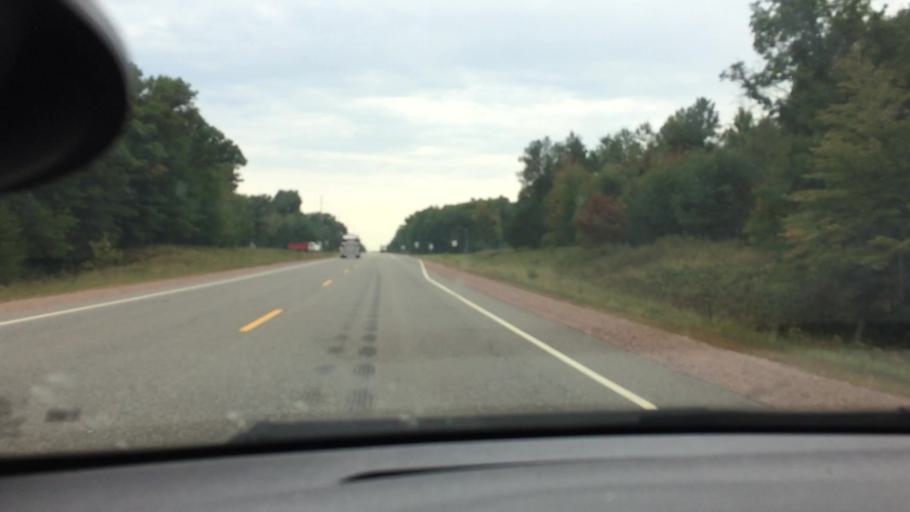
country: US
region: Wisconsin
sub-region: Clark County
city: Neillsville
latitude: 44.5714
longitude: -90.7285
